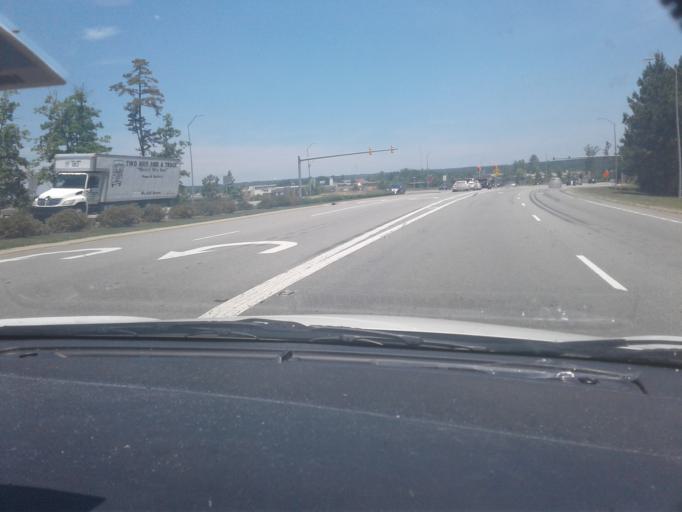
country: US
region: North Carolina
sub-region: Wake County
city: Holly Springs
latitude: 35.6598
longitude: -78.8482
